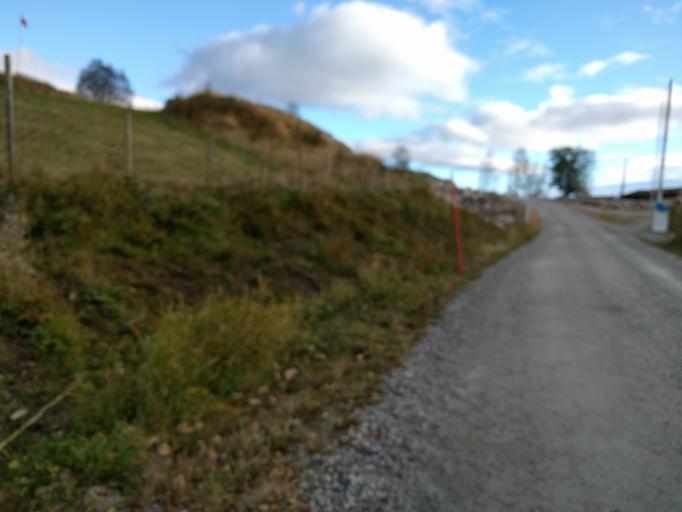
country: NO
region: Aust-Agder
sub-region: Evje og Hornnes
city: Evje
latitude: 58.6518
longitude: 7.9497
